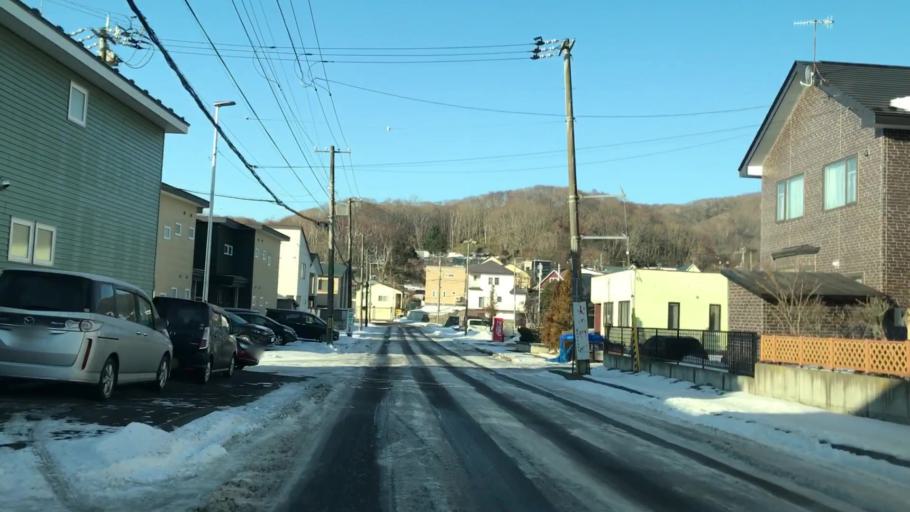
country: JP
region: Hokkaido
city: Muroran
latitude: 42.3892
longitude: 141.0673
